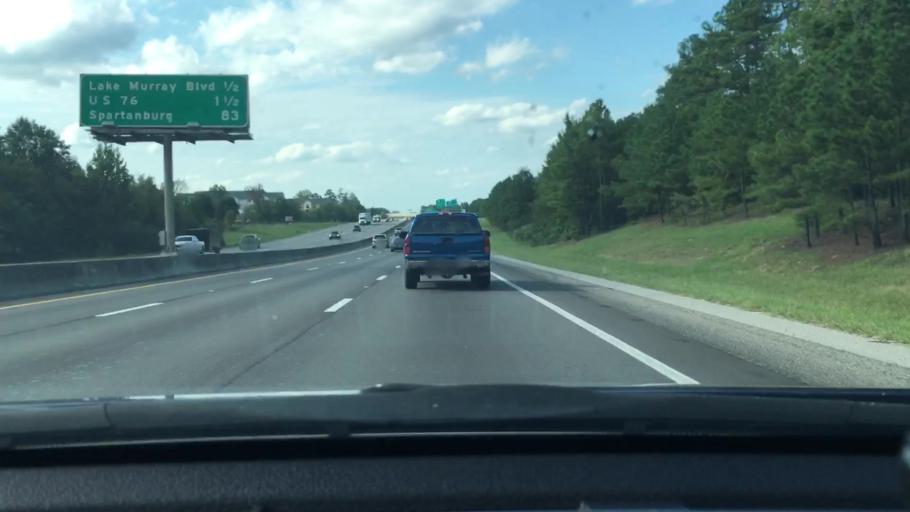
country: US
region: South Carolina
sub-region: Lexington County
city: Irmo
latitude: 34.0840
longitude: -81.1587
